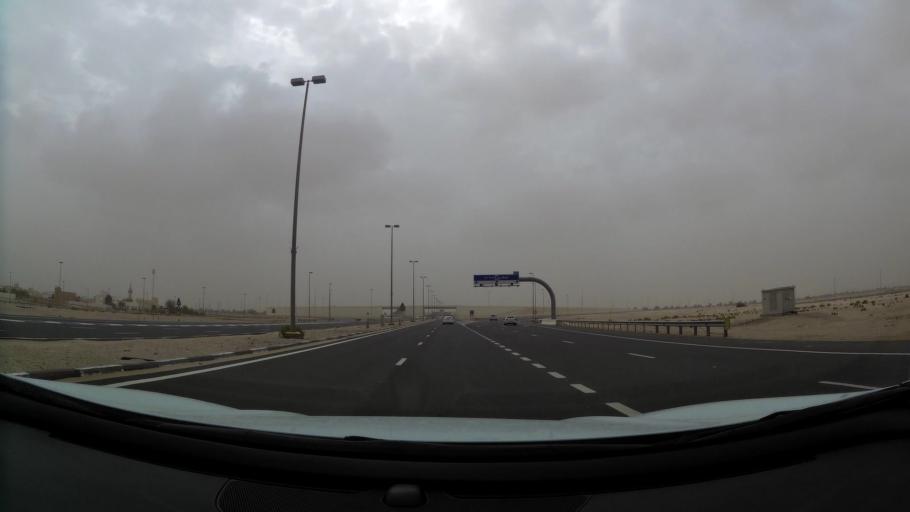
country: AE
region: Abu Dhabi
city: Abu Dhabi
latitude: 24.4214
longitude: 54.7133
